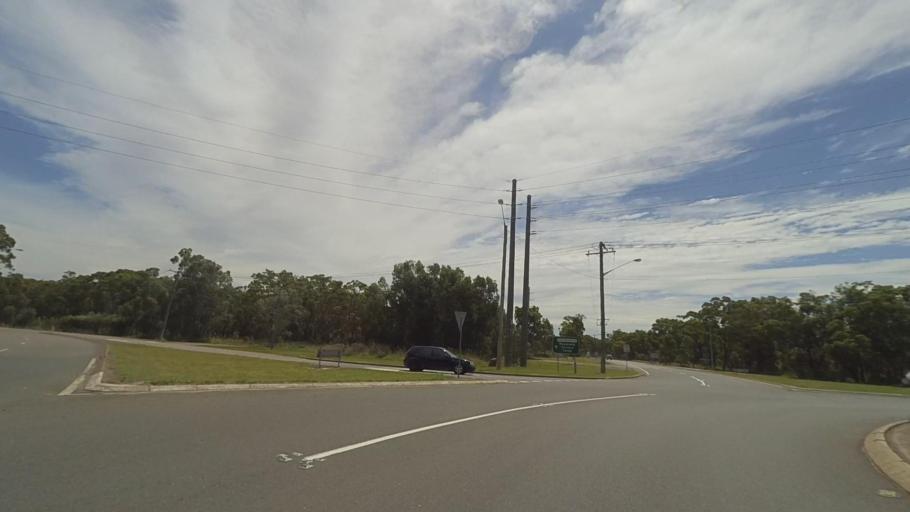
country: AU
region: New South Wales
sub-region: Port Stephens Shire
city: Medowie
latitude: -32.7724
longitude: 151.8599
